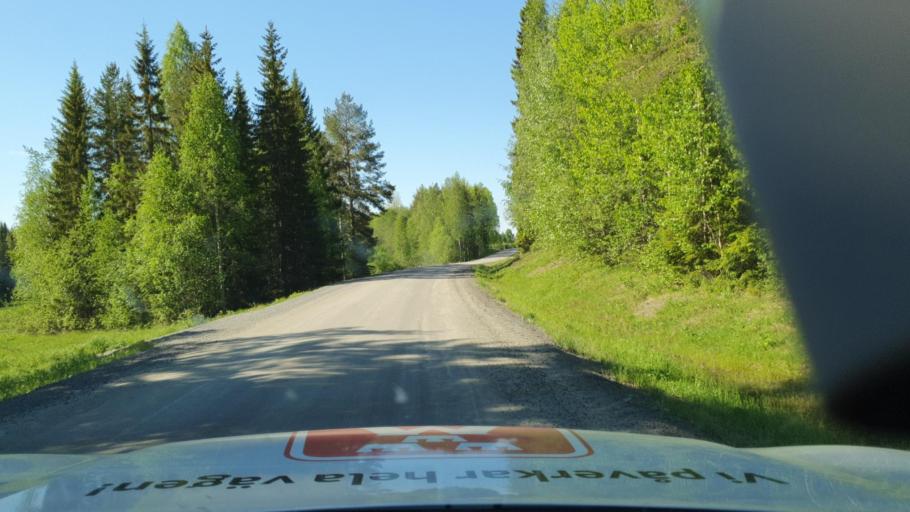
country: SE
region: Vaesterbotten
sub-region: Vannas Kommun
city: Vaennaes
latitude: 64.0177
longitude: 19.7484
